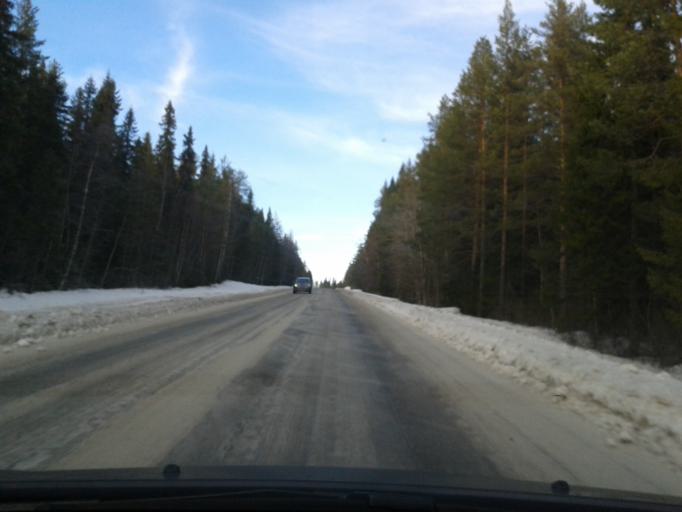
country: SE
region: Vaesternorrland
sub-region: OErnskoeldsviks Kommun
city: Bredbyn
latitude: 63.5889
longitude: 17.9221
